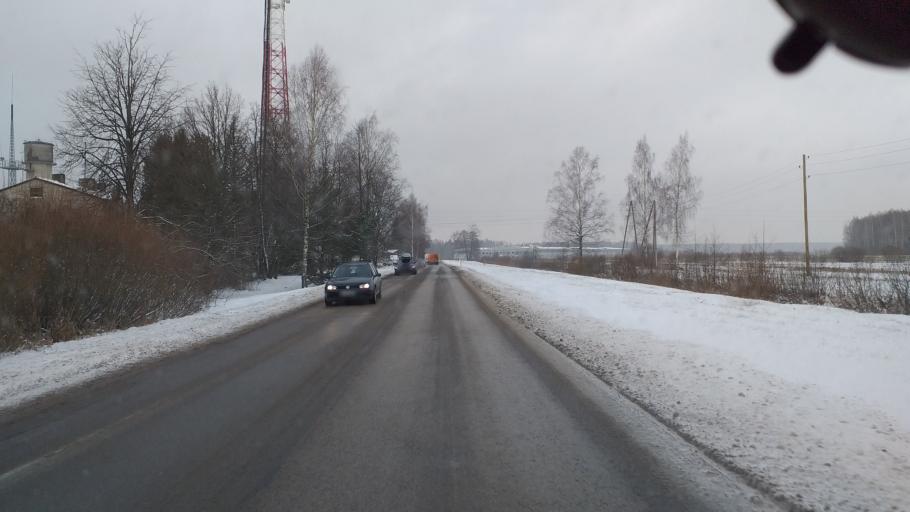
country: LV
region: Olaine
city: Olaine
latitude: 56.7976
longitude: 23.9351
